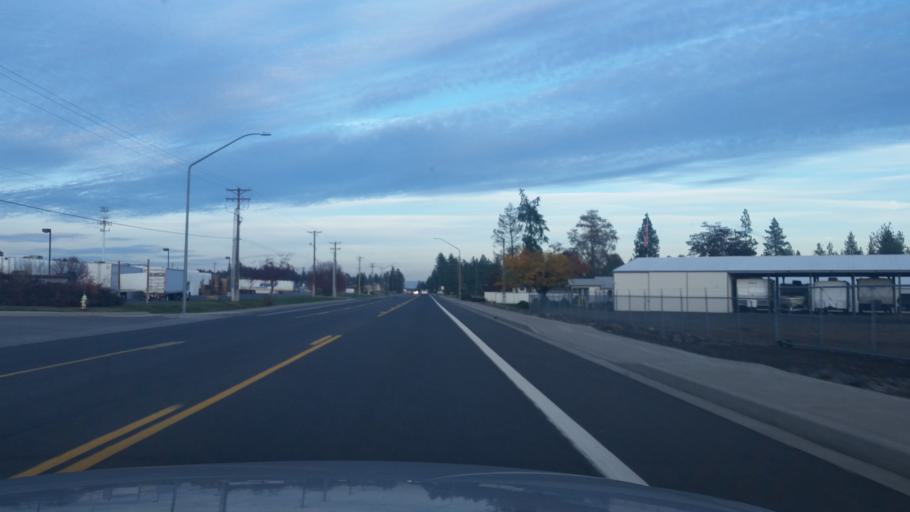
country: US
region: Washington
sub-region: Spokane County
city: Cheney
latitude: 47.4730
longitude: -117.6052
